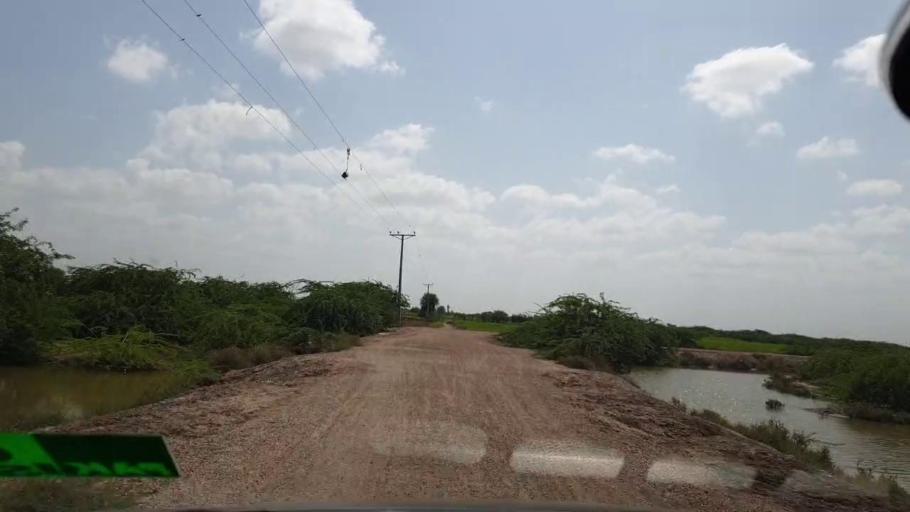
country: PK
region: Sindh
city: Kadhan
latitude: 24.5993
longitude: 69.1851
